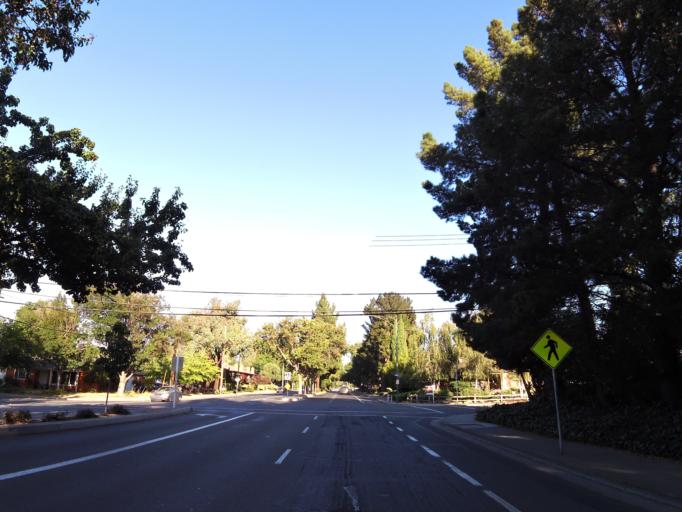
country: US
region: California
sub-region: Santa Clara County
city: Mountain View
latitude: 37.3986
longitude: -122.0654
